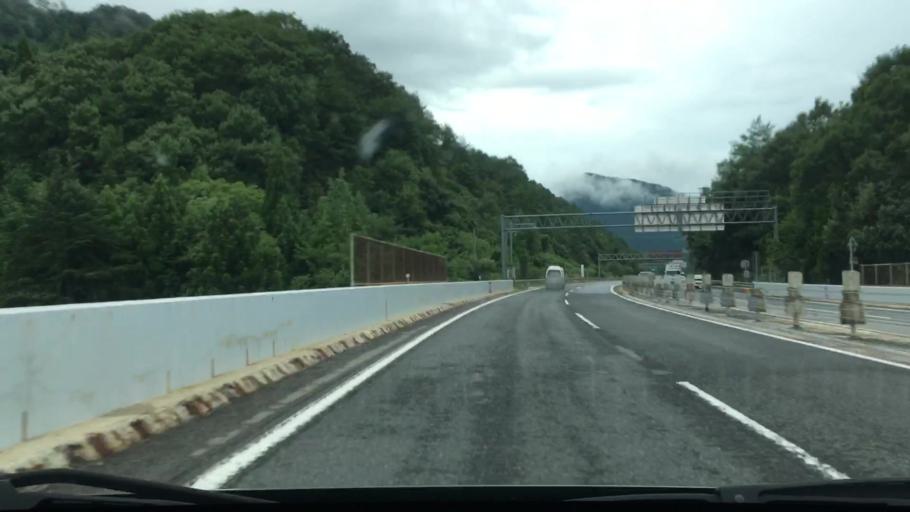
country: JP
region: Hiroshima
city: Hiroshima-shi
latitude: 34.5667
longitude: 132.4556
